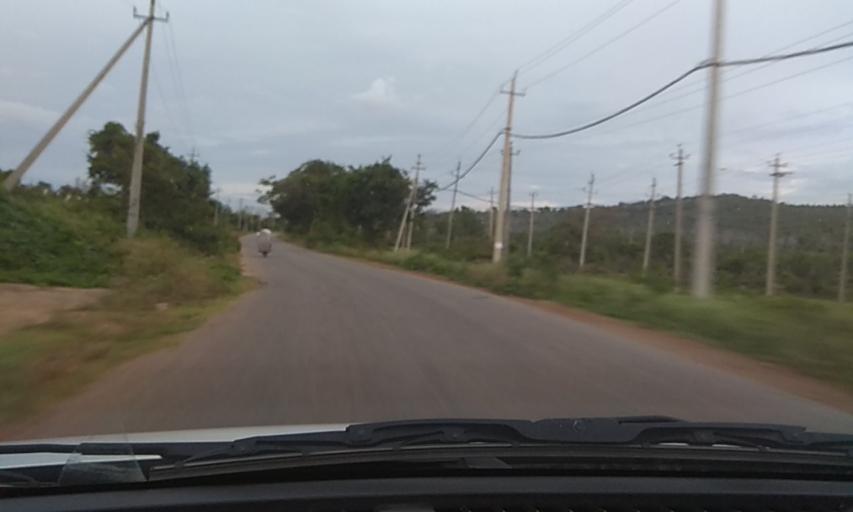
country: IN
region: Karnataka
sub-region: Chamrajnagar
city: Gundlupet
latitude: 11.8013
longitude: 76.7949
